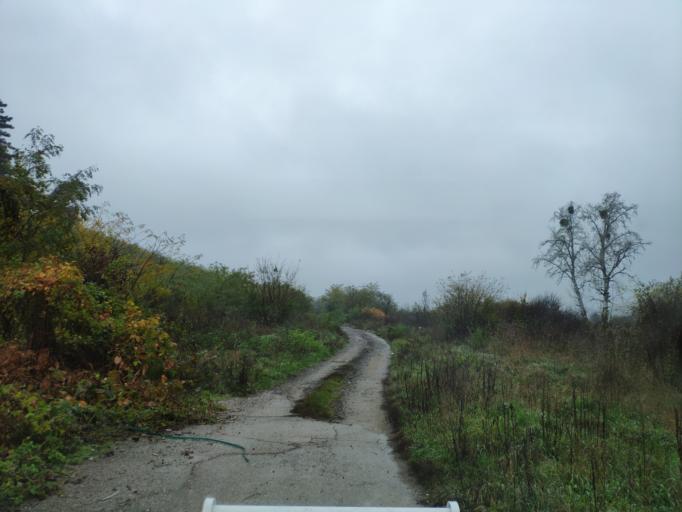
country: SK
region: Kosicky
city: Cierna nad Tisou
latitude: 48.4434
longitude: 21.9998
